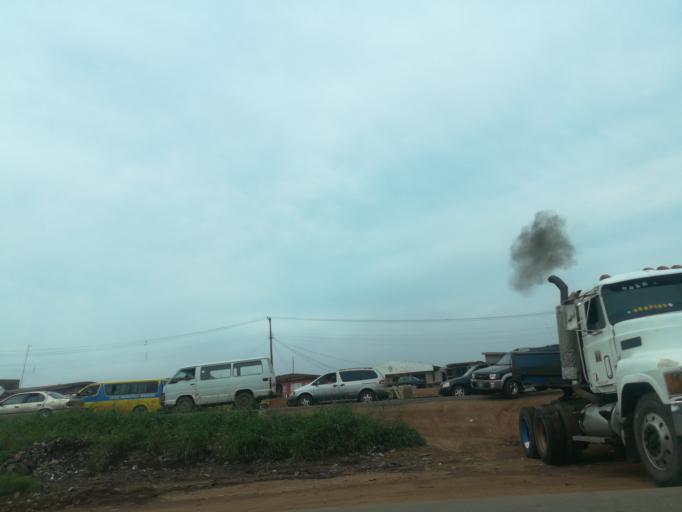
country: NG
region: Oyo
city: Ibadan
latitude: 7.3733
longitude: 3.9301
